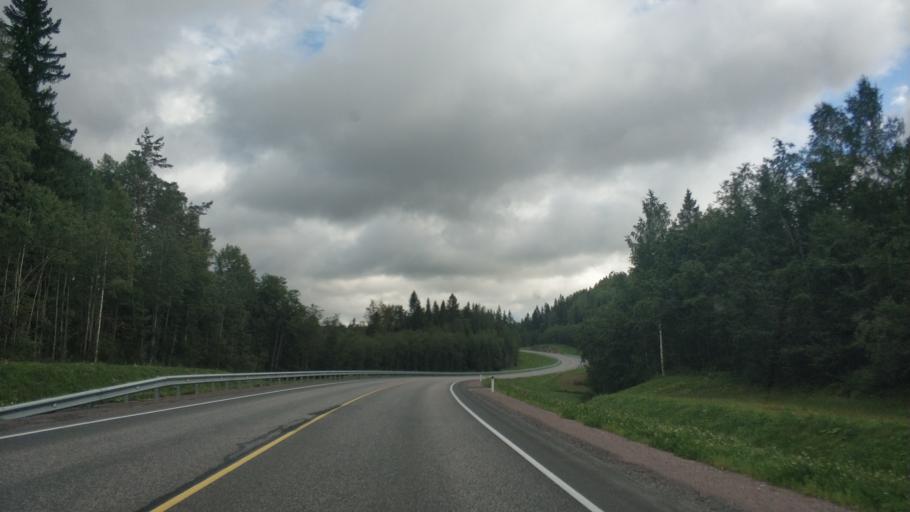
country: RU
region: Republic of Karelia
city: Khelyulya
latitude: 61.8302
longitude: 30.6354
